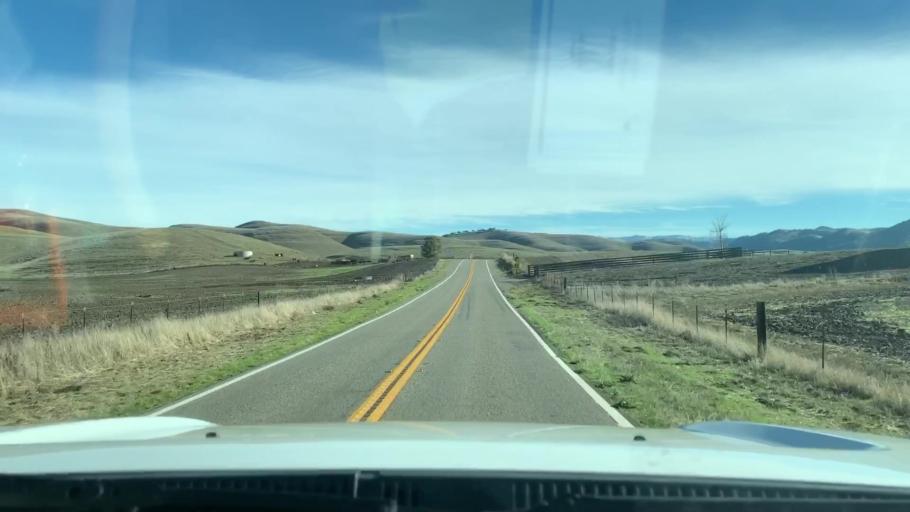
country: US
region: California
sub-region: Monterey County
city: King City
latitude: 36.1652
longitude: -120.8864
